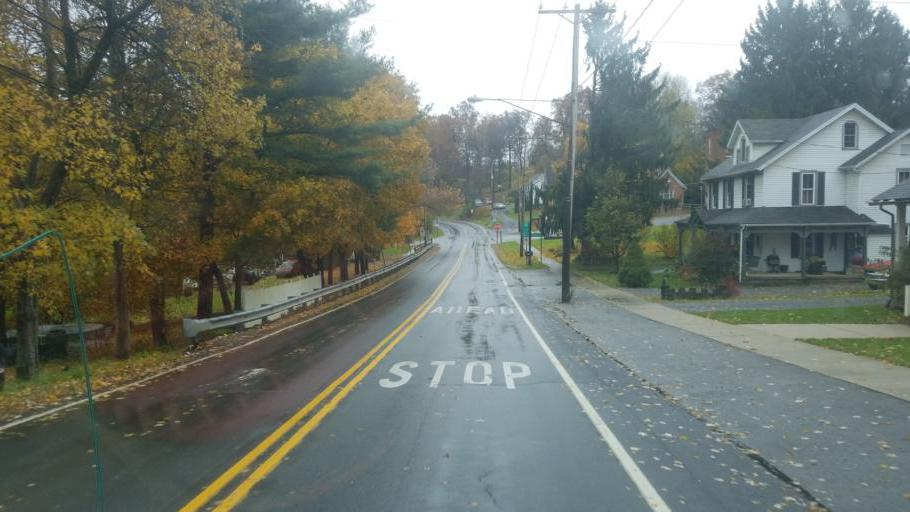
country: US
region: Pennsylvania
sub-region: Centre County
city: Milesburg
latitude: 41.0276
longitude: -77.9525
